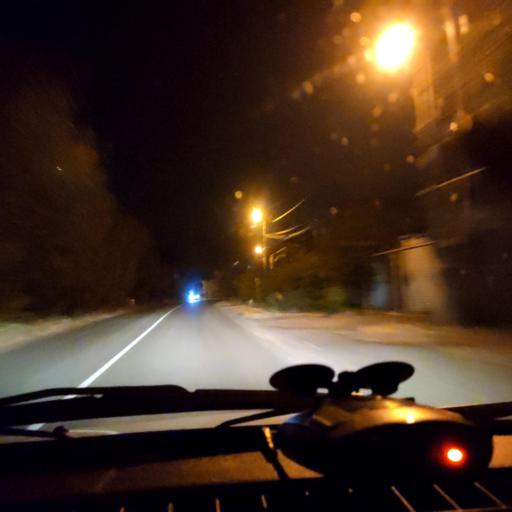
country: RU
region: Voronezj
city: Podgornoye
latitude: 51.7327
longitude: 39.1476
